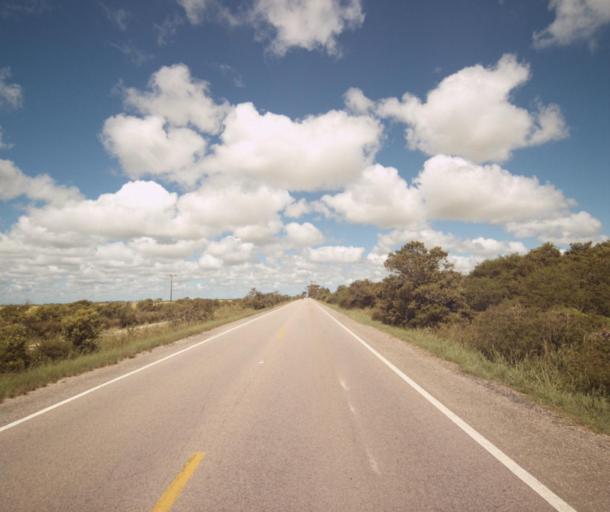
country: BR
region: Rio Grande do Sul
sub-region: Rio Grande
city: Rio Grande
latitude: -32.1906
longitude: -52.4336
